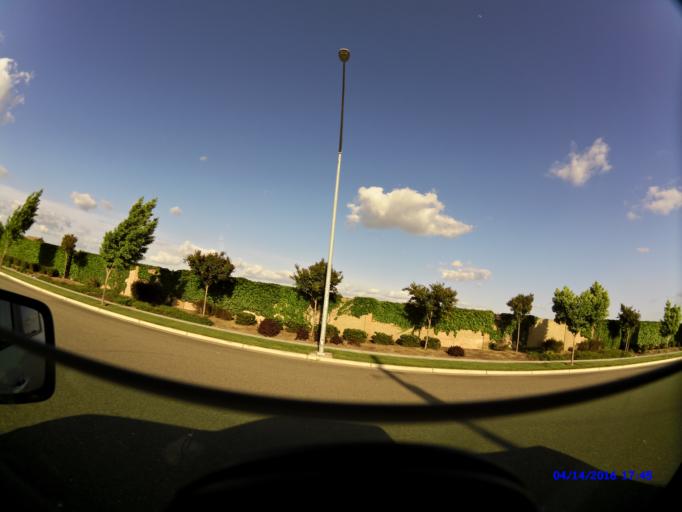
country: US
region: California
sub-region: Stanislaus County
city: Riverbank
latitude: 37.6825
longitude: -120.9578
